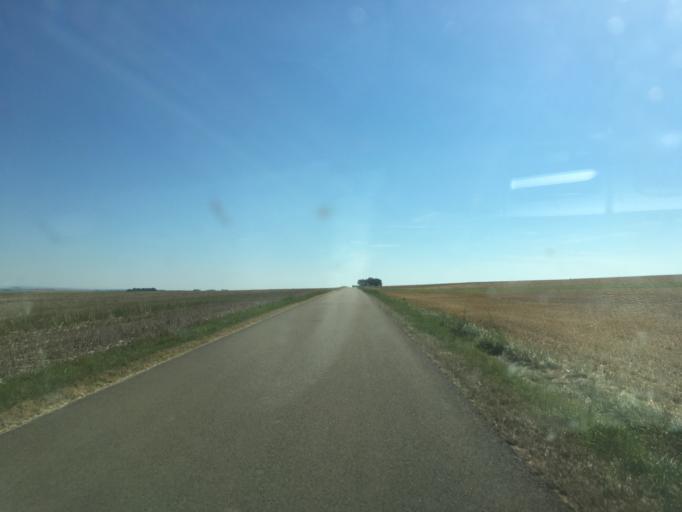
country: FR
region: Bourgogne
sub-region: Departement de l'Yonne
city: Aillant-sur-Tholon
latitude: 47.9162
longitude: 3.3814
